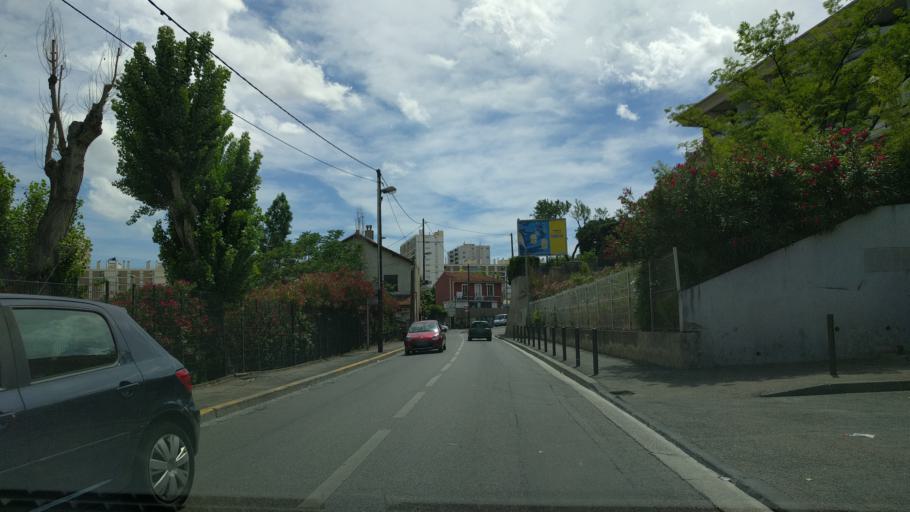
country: FR
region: Provence-Alpes-Cote d'Azur
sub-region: Departement des Bouches-du-Rhone
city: Marseille 13
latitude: 43.3319
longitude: 5.4065
